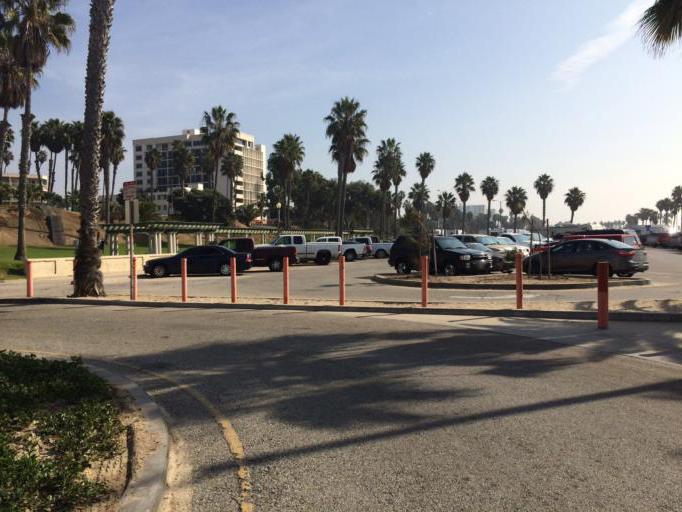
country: US
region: California
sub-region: Los Angeles County
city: Santa Monica
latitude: 34.0056
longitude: -118.4912
